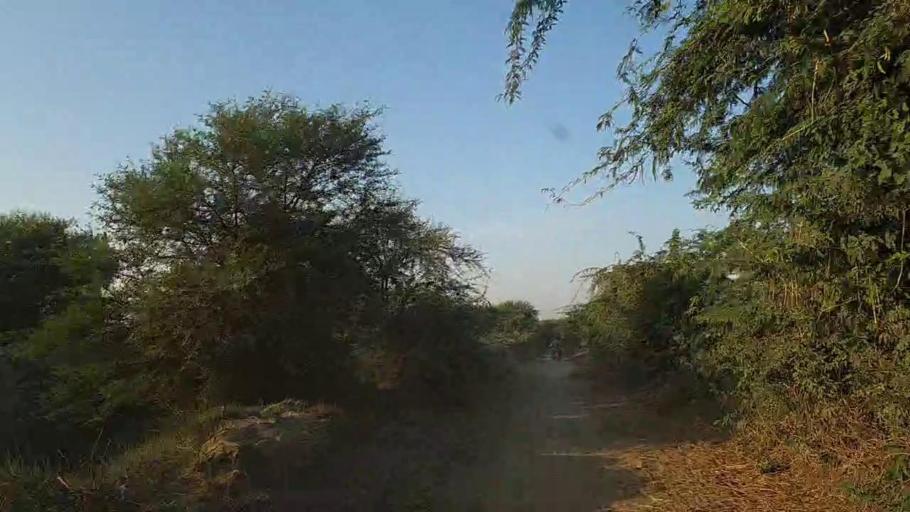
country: PK
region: Sindh
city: Mirpur Batoro
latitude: 24.7160
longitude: 68.2147
